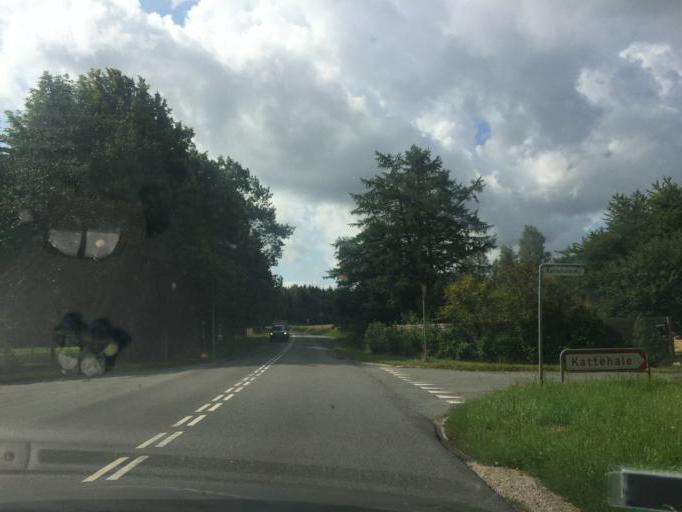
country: DK
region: Capital Region
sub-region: Allerod Kommune
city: Blovstrod
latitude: 55.8489
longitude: 12.3892
